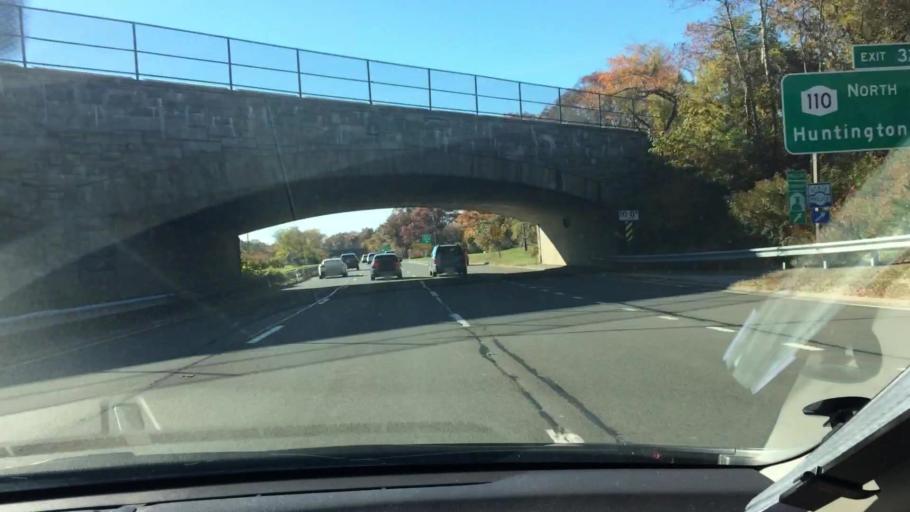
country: US
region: New York
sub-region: Suffolk County
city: North Amityville
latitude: 40.7080
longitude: -73.4239
